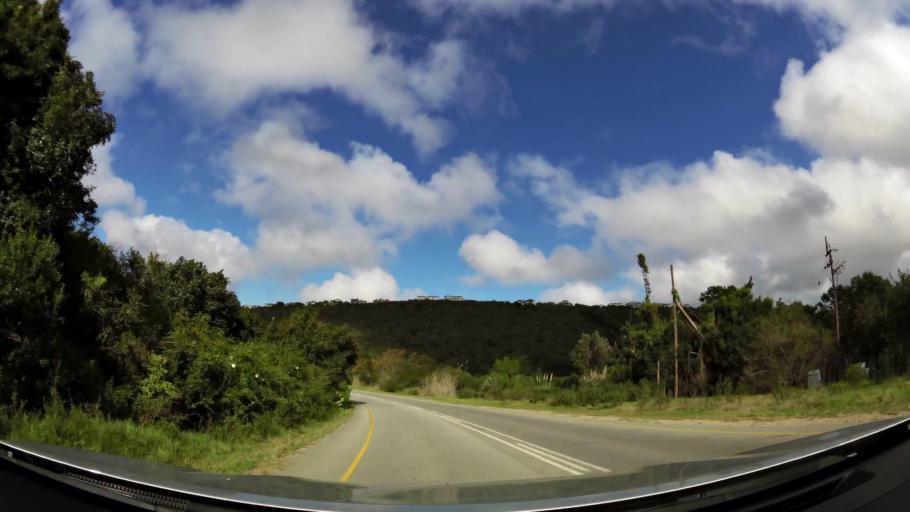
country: ZA
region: Western Cape
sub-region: Eden District Municipality
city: Plettenberg Bay
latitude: -34.0612
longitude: 23.3547
